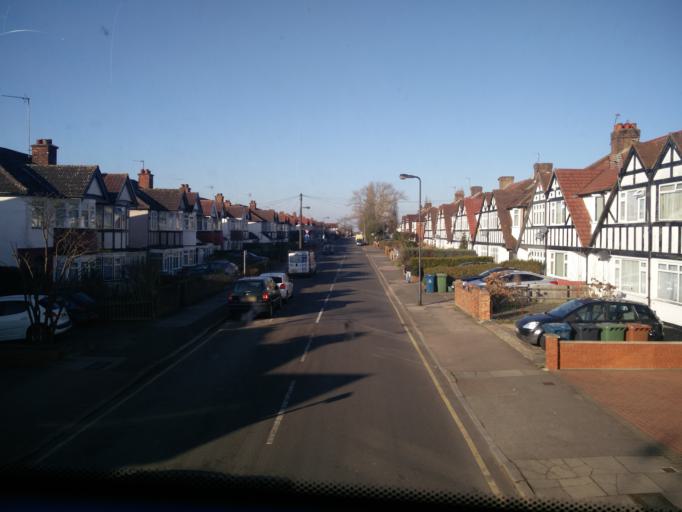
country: GB
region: England
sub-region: Greater London
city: Northolt
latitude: 51.5727
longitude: -0.3663
